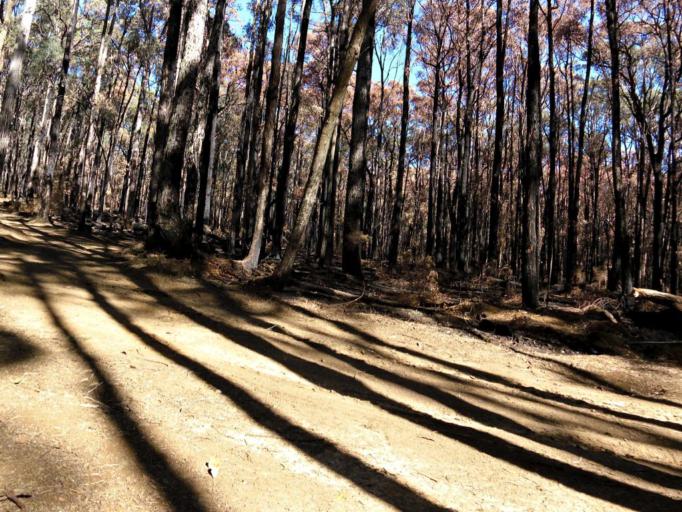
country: AU
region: Victoria
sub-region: Cardinia
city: Cockatoo
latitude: -37.9352
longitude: 145.4753
